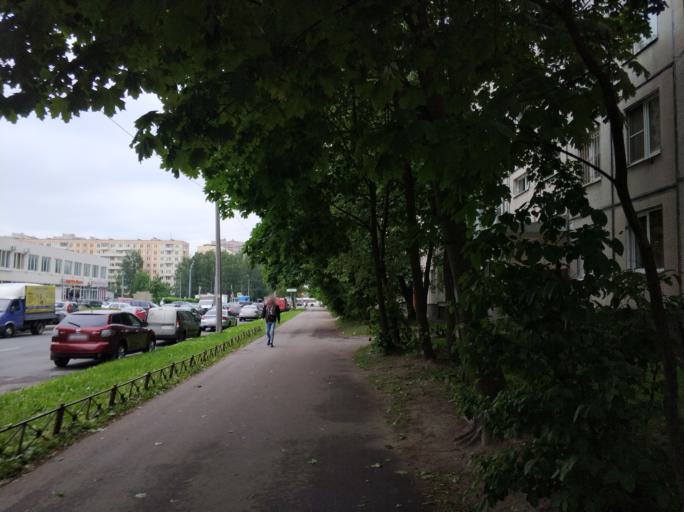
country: RU
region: St.-Petersburg
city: Grazhdanka
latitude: 60.0346
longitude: 30.3911
